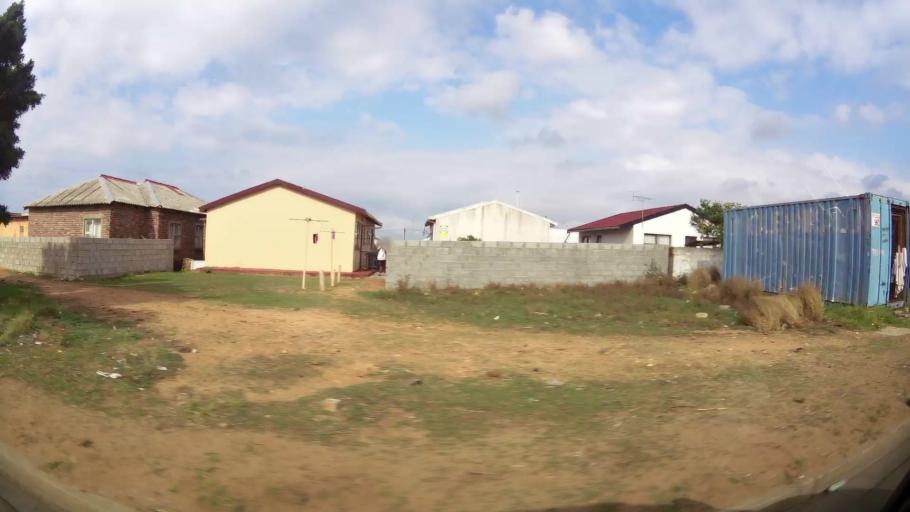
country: ZA
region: Eastern Cape
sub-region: Nelson Mandela Bay Metropolitan Municipality
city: Port Elizabeth
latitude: -33.8163
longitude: 25.5845
